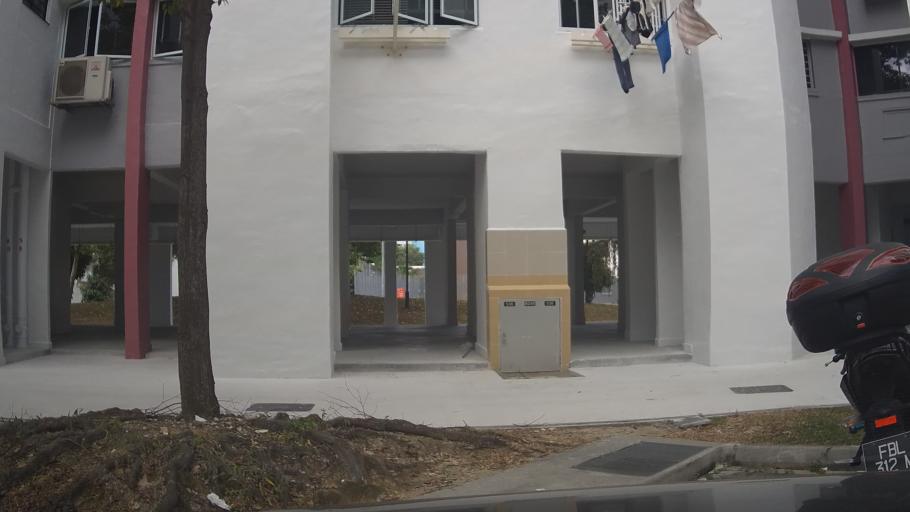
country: SG
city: Singapore
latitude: 1.3521
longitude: 103.9483
